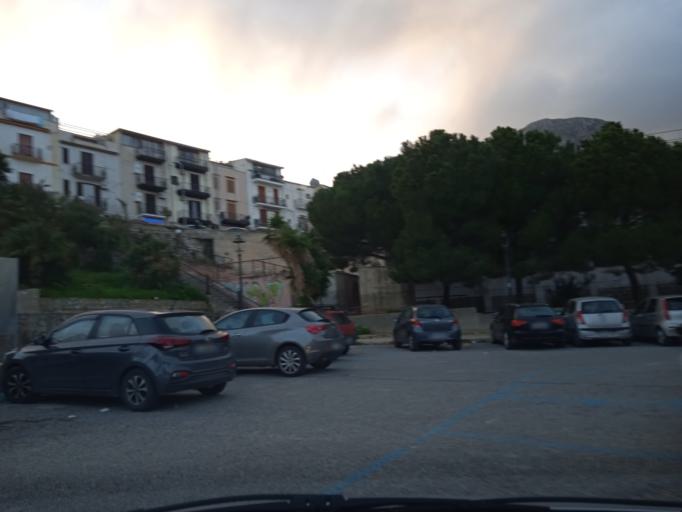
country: IT
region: Sicily
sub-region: Palermo
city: Santa Flavia
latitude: 38.0954
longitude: 13.5384
